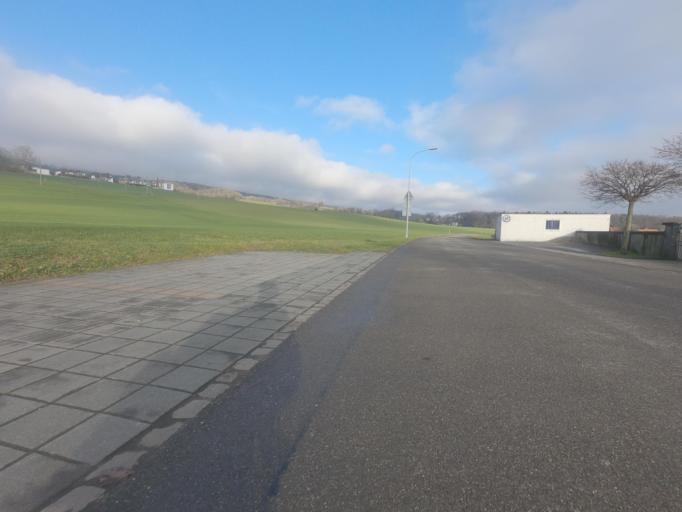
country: CH
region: Solothurn
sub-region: Bezirk Lebern
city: Bettlach
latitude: 47.2017
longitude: 7.4303
